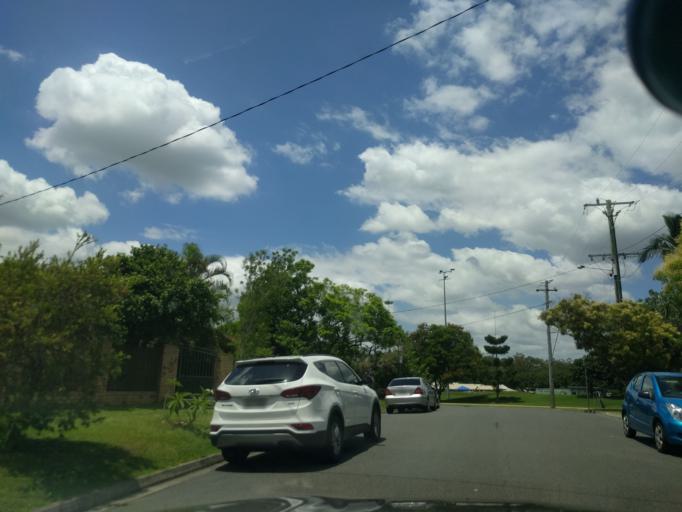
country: AU
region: Queensland
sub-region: Brisbane
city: South Brisbane
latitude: -27.4936
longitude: 153.0081
